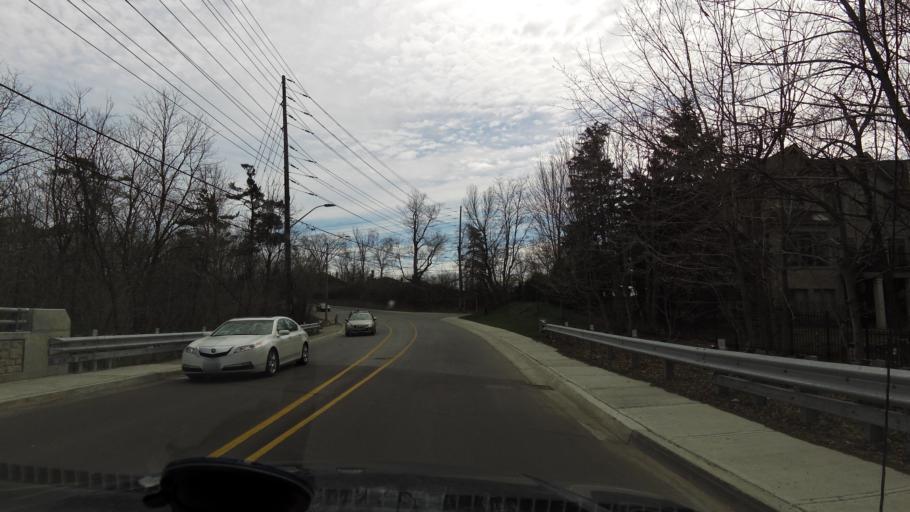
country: CA
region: Ontario
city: Mississauga
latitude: 43.5549
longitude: -79.6782
